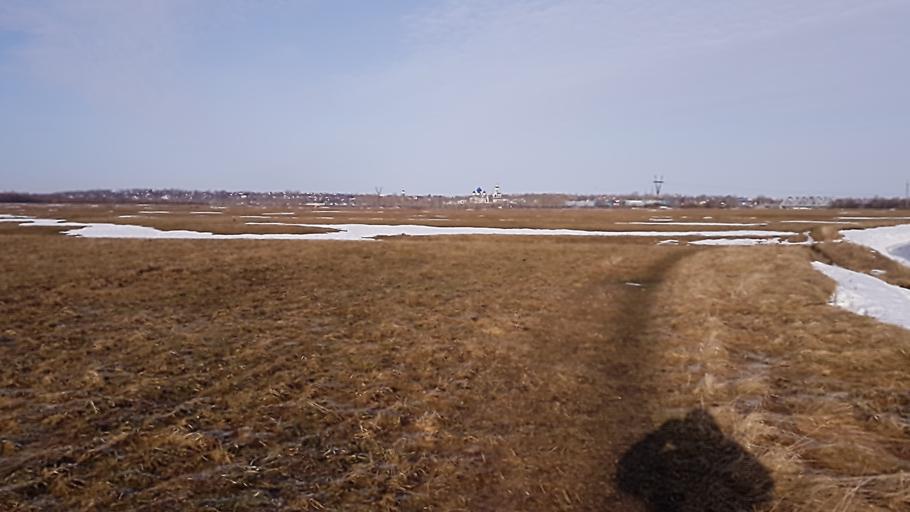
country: RU
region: Vladimir
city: Bogolyubovo
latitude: 56.1908
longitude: 40.5665
